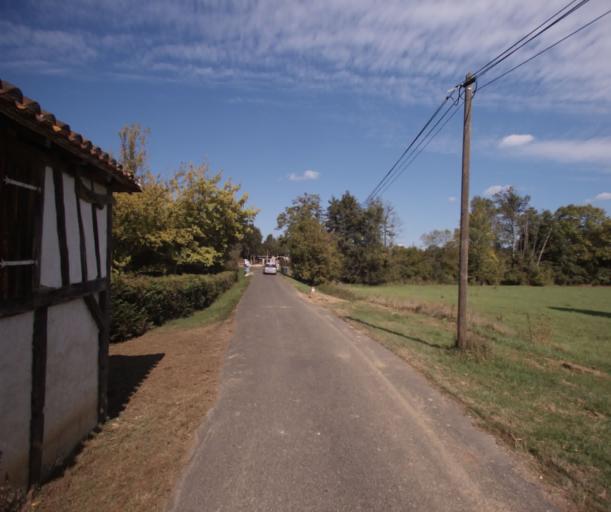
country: FR
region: Midi-Pyrenees
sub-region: Departement du Gers
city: Cazaubon
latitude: 43.9445
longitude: -0.0714
